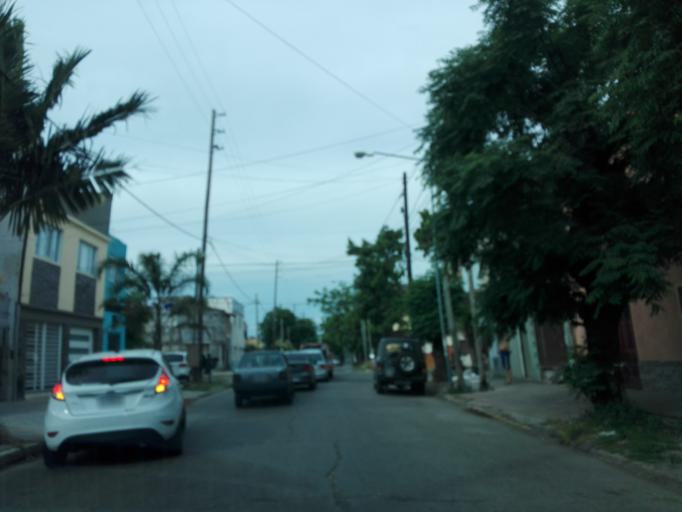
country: AR
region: Buenos Aires
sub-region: Partido de Lanus
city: Lanus
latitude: -34.7220
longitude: -58.3849
